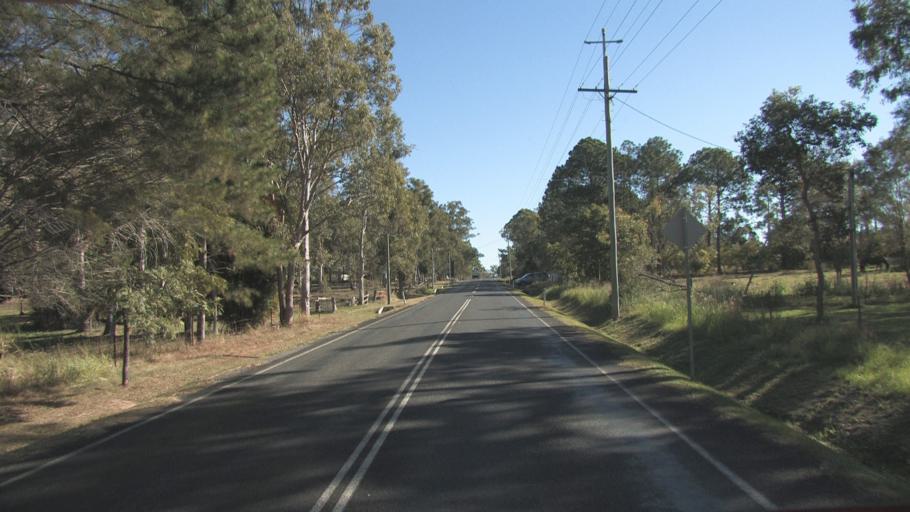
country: AU
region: Queensland
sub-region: Logan
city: Park Ridge South
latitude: -27.7235
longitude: 153.0174
